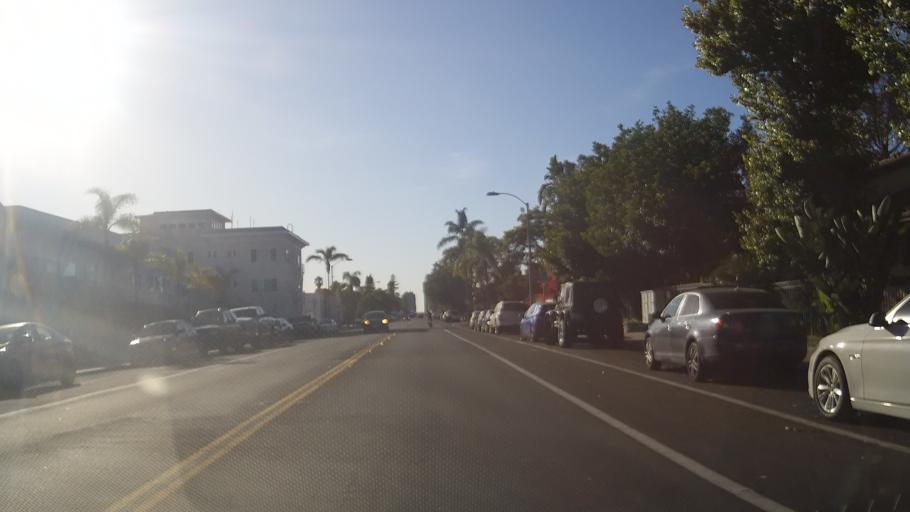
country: US
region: California
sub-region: San Diego County
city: San Diego
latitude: 32.7179
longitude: -117.1350
